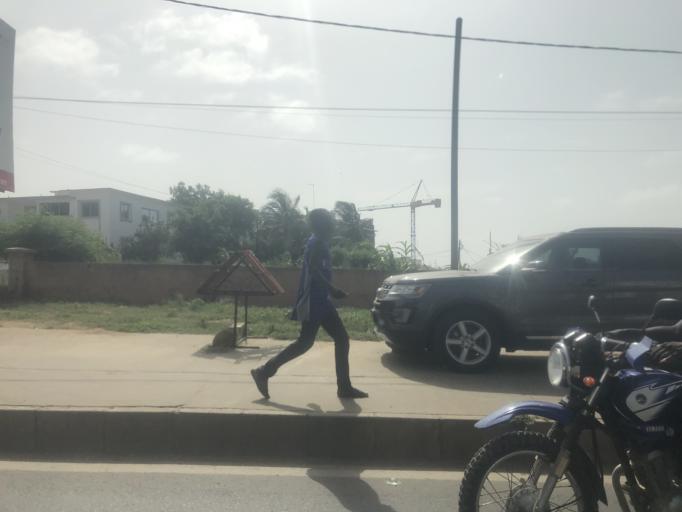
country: SN
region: Dakar
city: Mermoz Boabab
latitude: 14.7401
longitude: -17.5104
